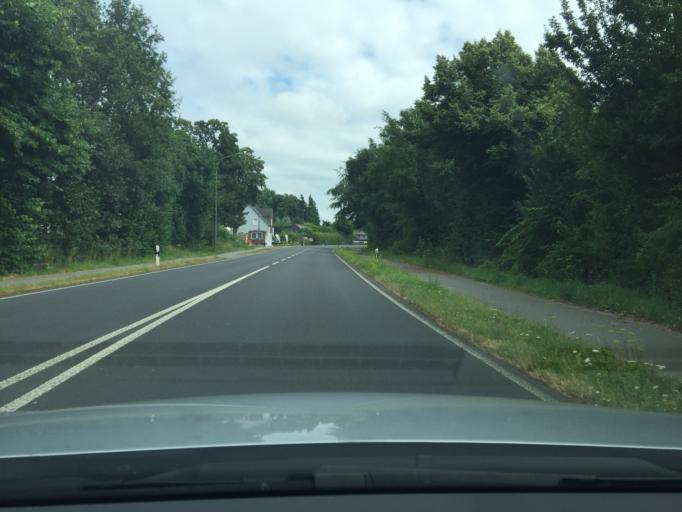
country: DE
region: North Rhine-Westphalia
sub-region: Regierungsbezirk Dusseldorf
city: Heiligenhaus
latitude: 51.3320
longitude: 6.9335
